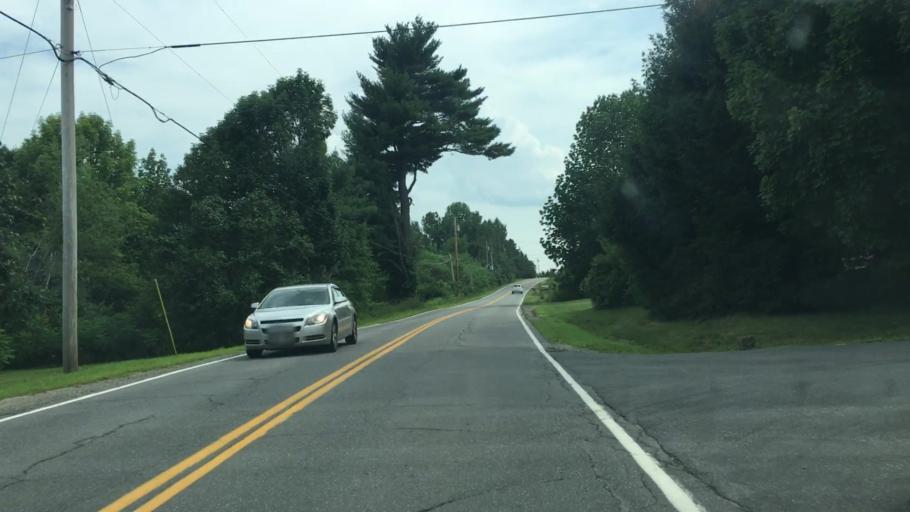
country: US
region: Maine
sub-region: Kennebec County
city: China
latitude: 44.4249
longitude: -69.5884
